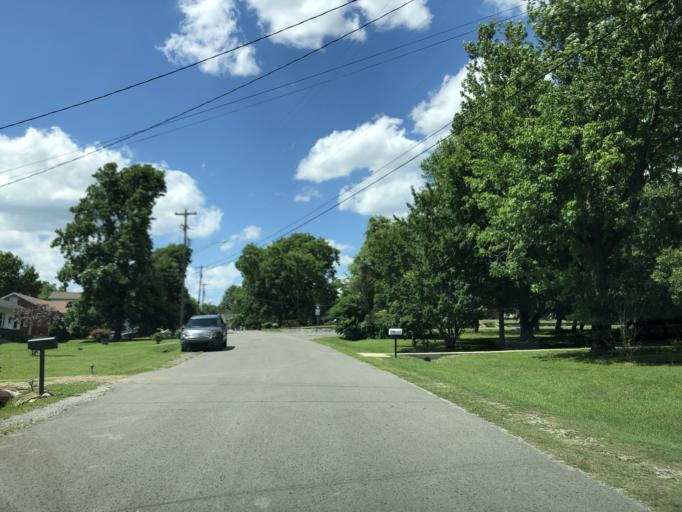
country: US
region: Tennessee
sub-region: Davidson County
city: Nashville
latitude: 36.1772
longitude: -86.7209
